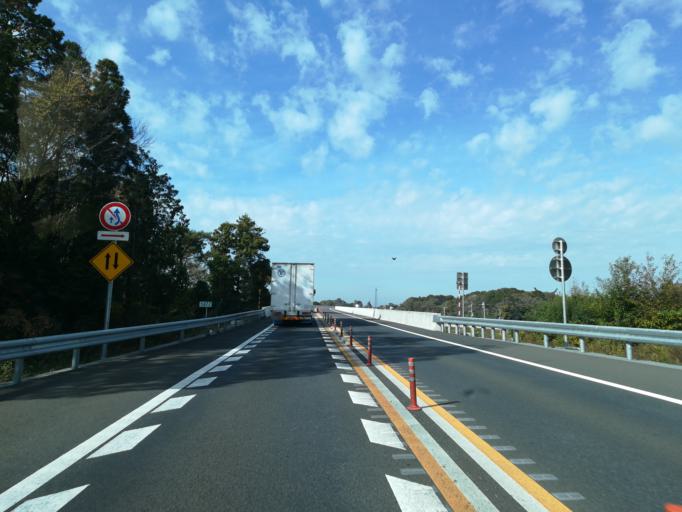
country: JP
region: Ibaraki
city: Mitsukaido
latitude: 36.0678
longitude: 140.0220
